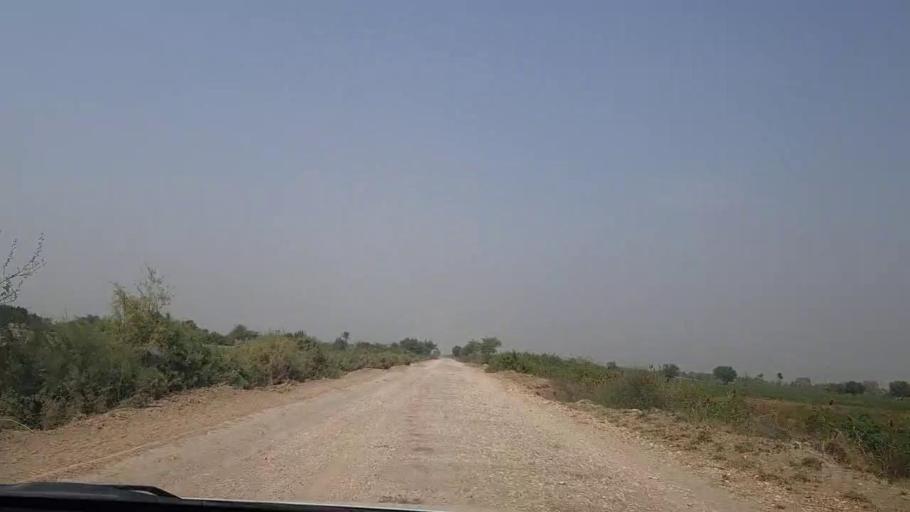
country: PK
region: Sindh
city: Mirpur Khas
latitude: 25.5932
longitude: 69.2010
